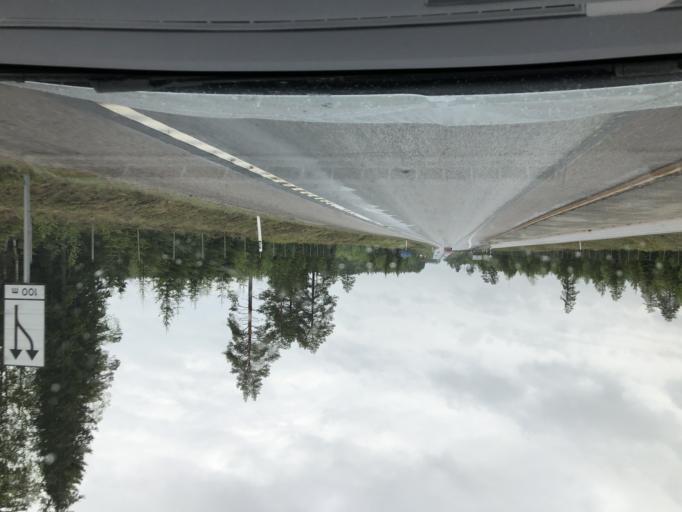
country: SE
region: Vaesterbotten
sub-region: Umea Kommun
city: Hoernefors
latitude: 63.6417
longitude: 19.9253
